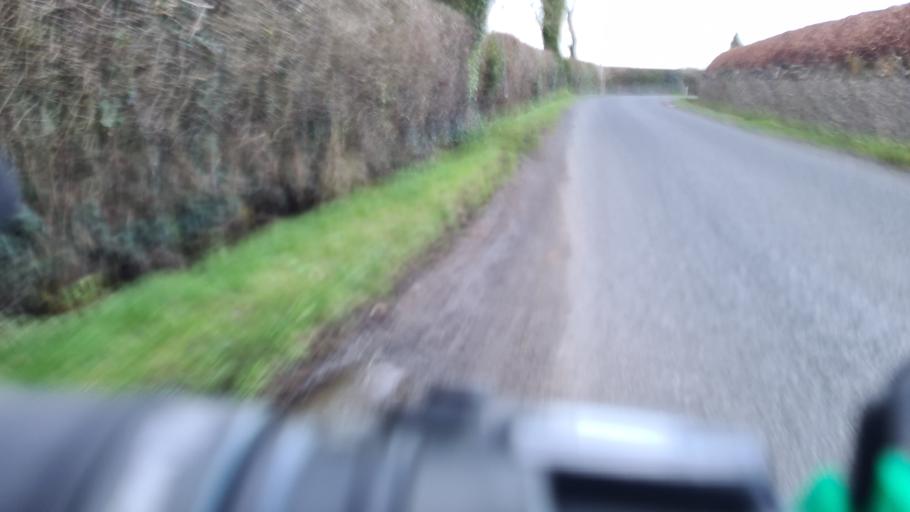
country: IE
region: Leinster
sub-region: Kildare
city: Maynooth
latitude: 53.3392
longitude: -6.5951
